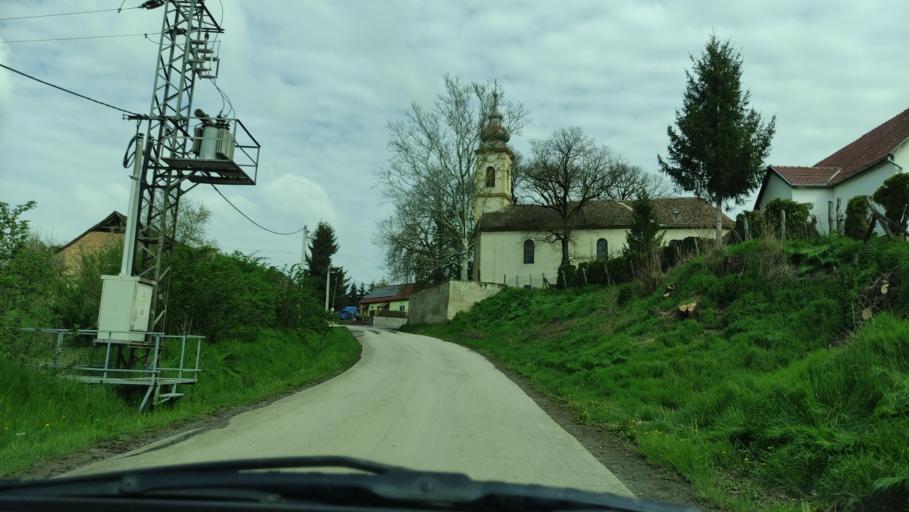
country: HU
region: Baranya
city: Magocs
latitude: 46.2735
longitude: 18.2154
